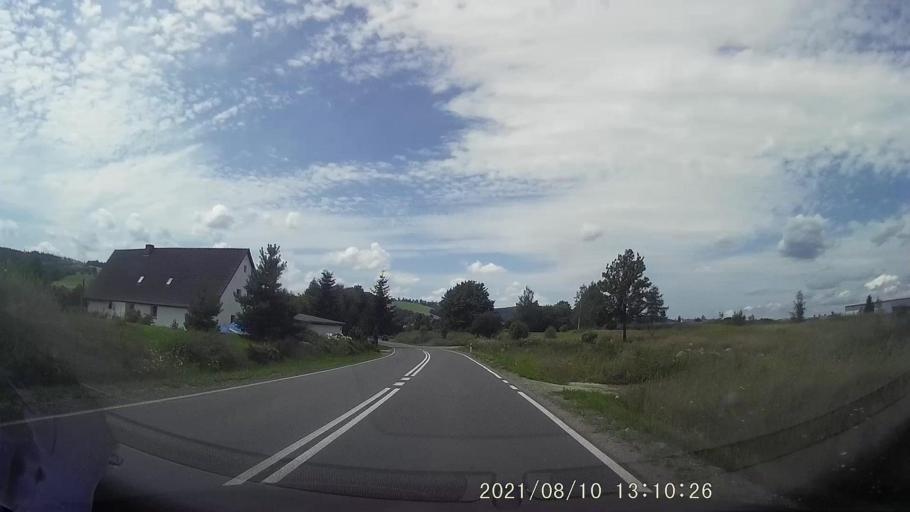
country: PL
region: Lower Silesian Voivodeship
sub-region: Powiat klodzki
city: Bozkow
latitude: 50.5030
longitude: 16.5295
